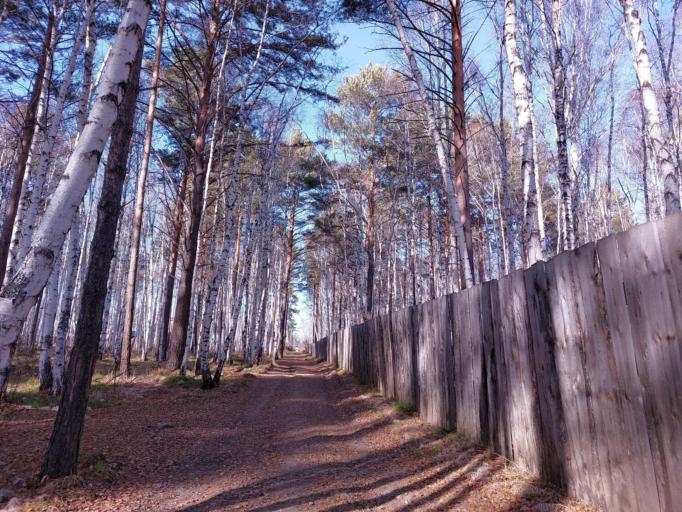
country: RU
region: Irkutsk
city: Pivovarikha
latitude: 52.1846
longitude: 104.4567
